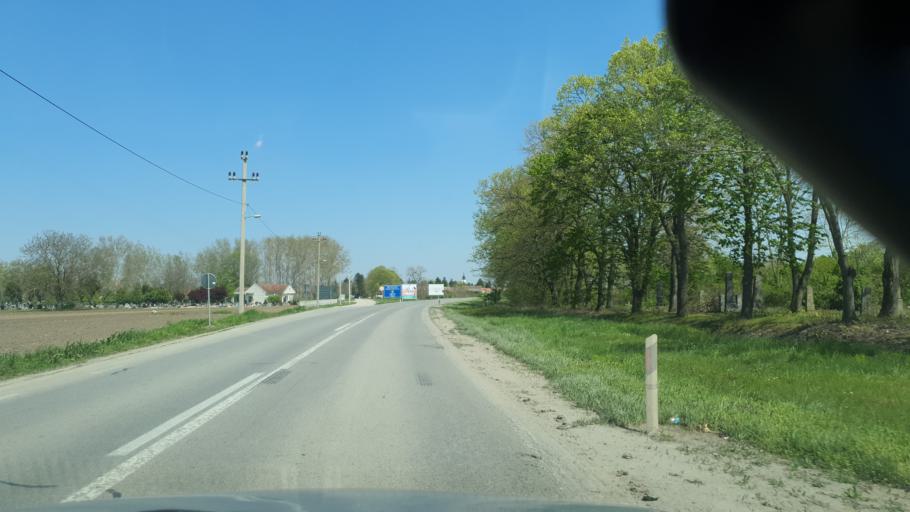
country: RS
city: Glozan
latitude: 45.2742
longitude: 19.5529
